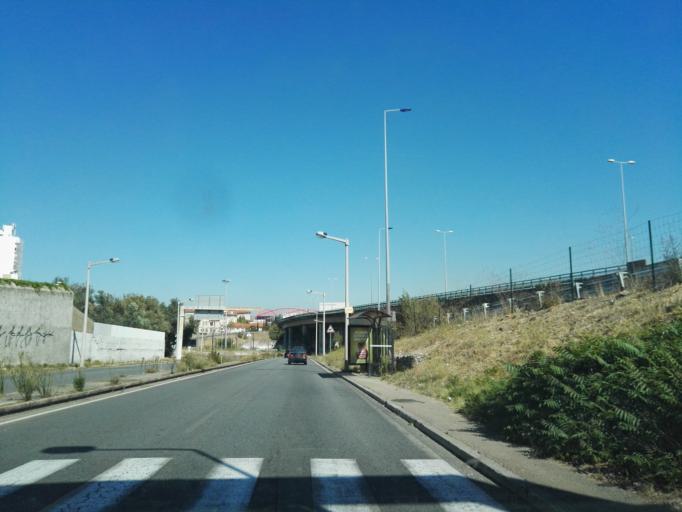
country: PT
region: Lisbon
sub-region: Odivelas
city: Pontinha
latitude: 38.7430
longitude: -9.1985
